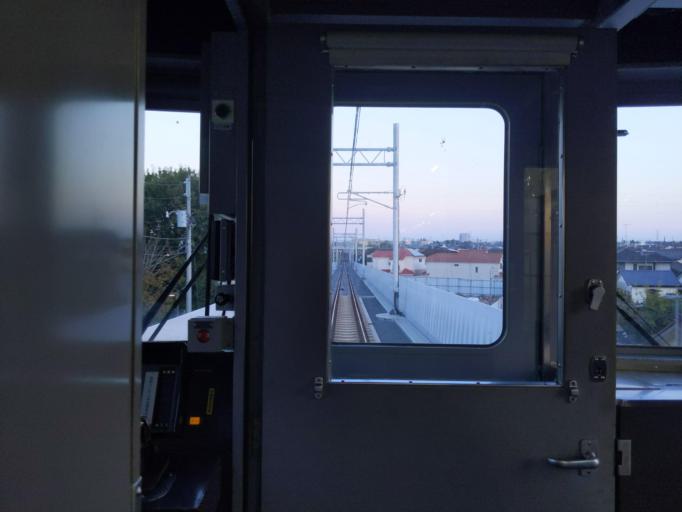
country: JP
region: Chiba
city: Noda
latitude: 35.9402
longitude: 139.8776
